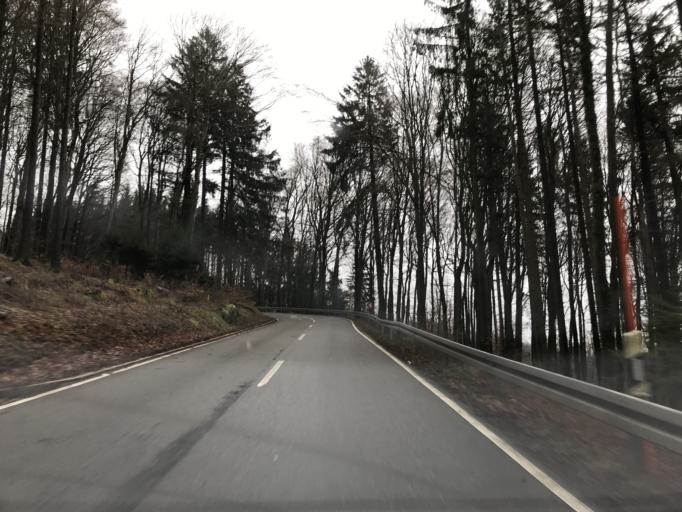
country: DE
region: Baden-Wuerttemberg
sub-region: Freiburg Region
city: Rickenbach
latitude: 47.6098
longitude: 7.9404
